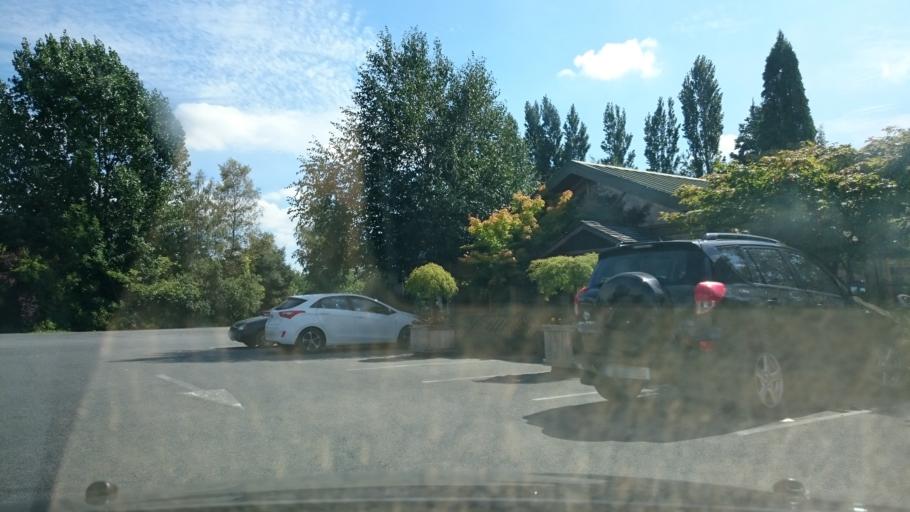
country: IE
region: Leinster
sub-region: Kilkenny
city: Thomastown
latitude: 52.6471
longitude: -7.1156
